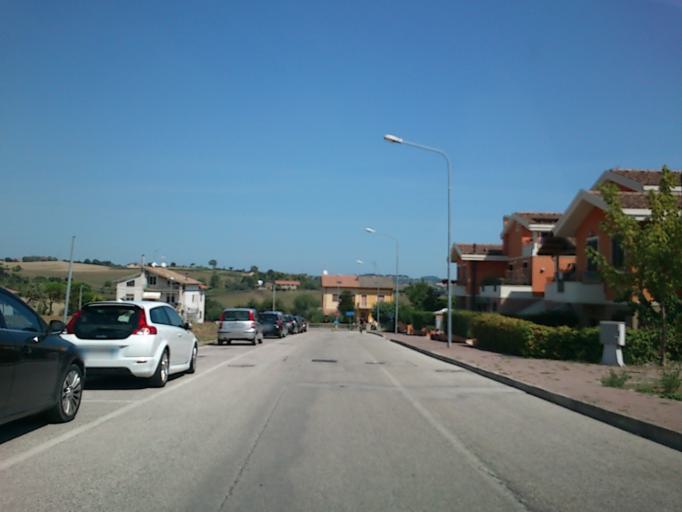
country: IT
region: The Marches
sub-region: Provincia di Pesaro e Urbino
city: Lucrezia
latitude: 43.7723
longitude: 12.9231
